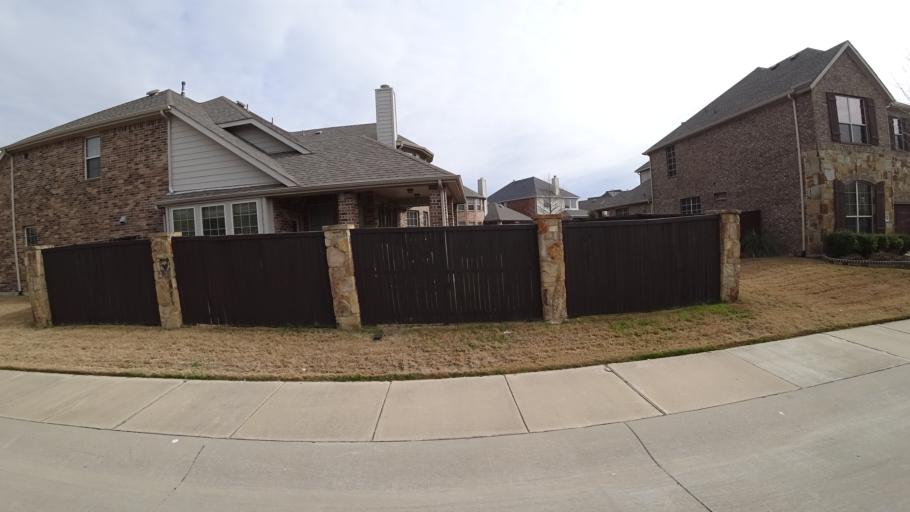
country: US
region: Texas
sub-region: Denton County
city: The Colony
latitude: 33.0527
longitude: -96.9089
